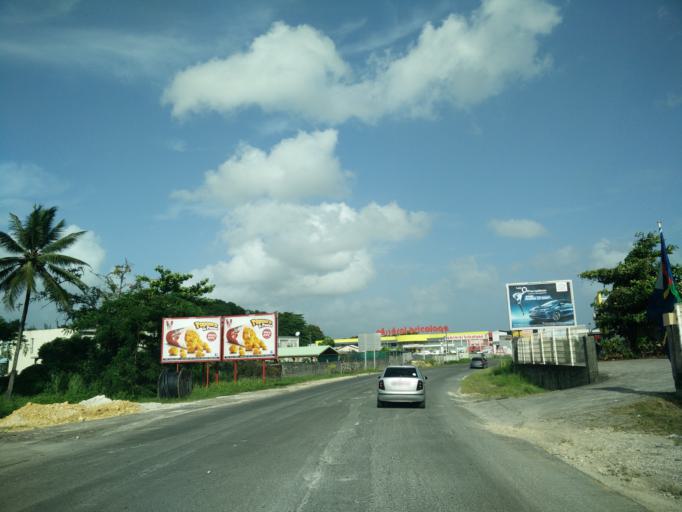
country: GP
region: Guadeloupe
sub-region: Guadeloupe
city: Les Abymes
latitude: 16.2561
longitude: -61.5140
